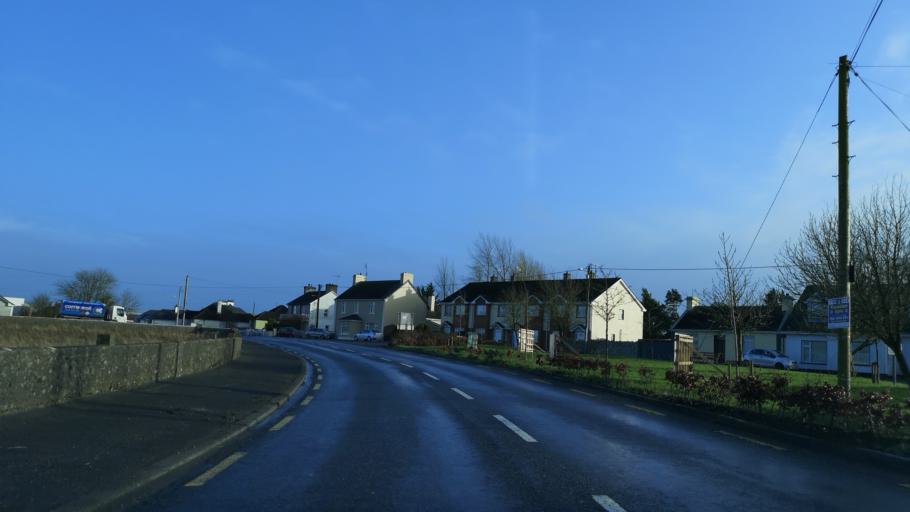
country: IE
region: Connaught
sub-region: County Galway
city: Tuam
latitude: 53.5065
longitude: -8.8374
